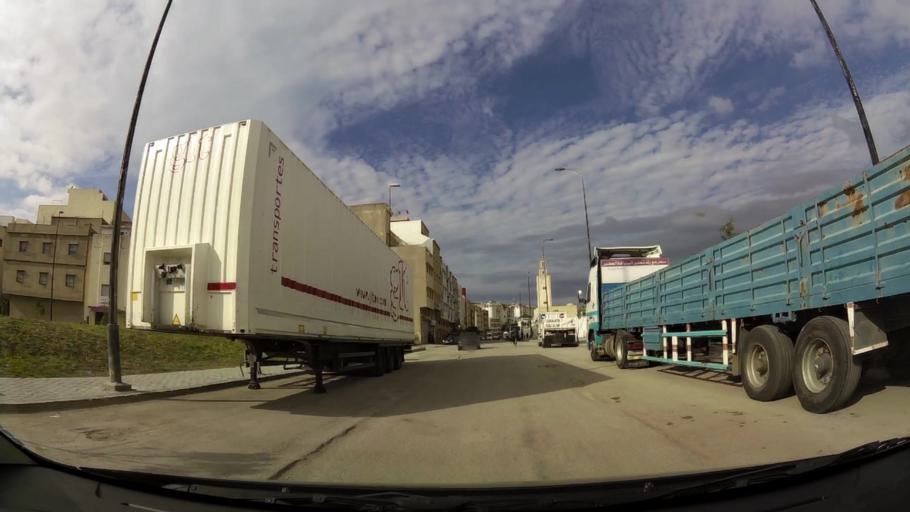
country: MA
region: Tanger-Tetouan
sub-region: Tanger-Assilah
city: Tangier
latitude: 35.7514
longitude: -5.7943
